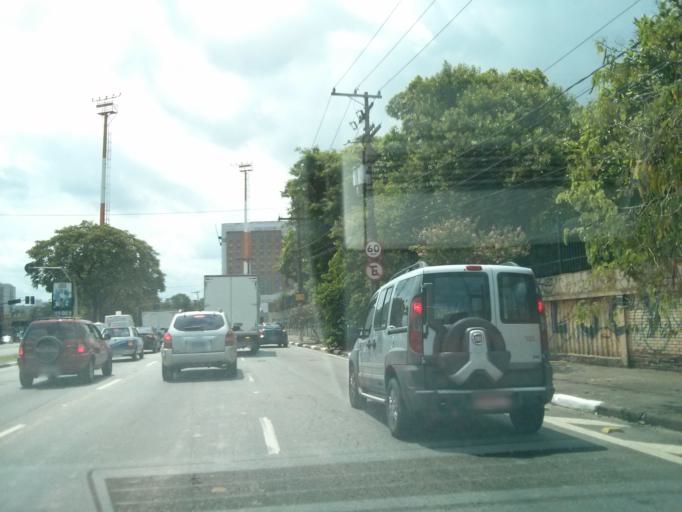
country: BR
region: Sao Paulo
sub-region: Sao Paulo
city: Sao Paulo
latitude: -23.6168
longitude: -46.6627
